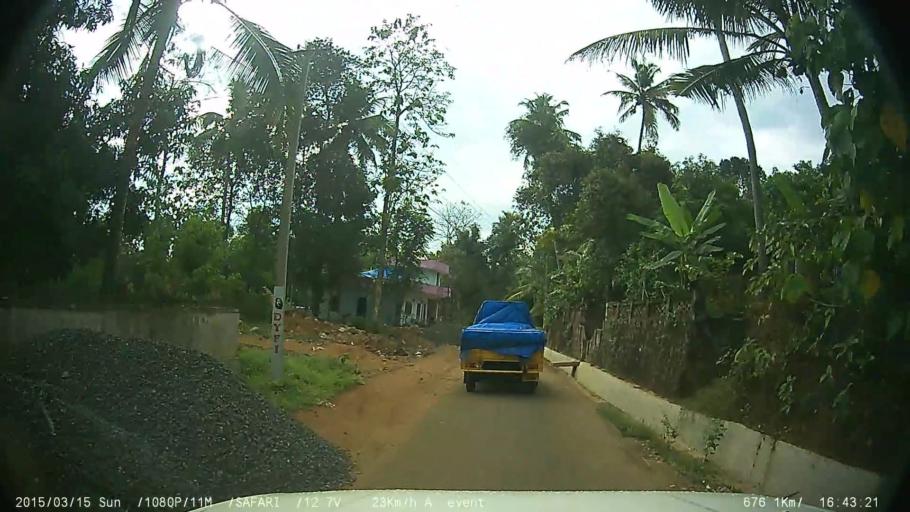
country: IN
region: Kerala
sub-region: Ernakulam
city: Piravam
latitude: 9.8581
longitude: 76.6032
